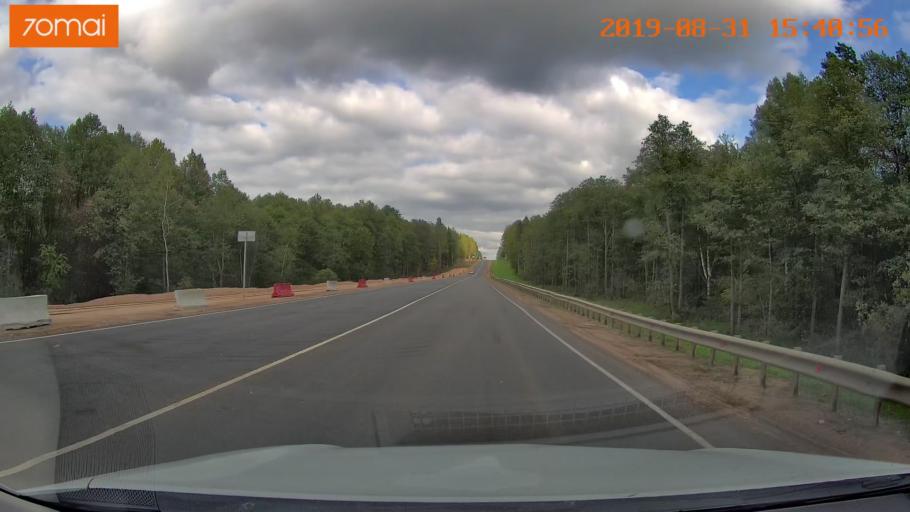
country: RU
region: Kaluga
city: Mosal'sk
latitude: 54.6357
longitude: 34.8479
